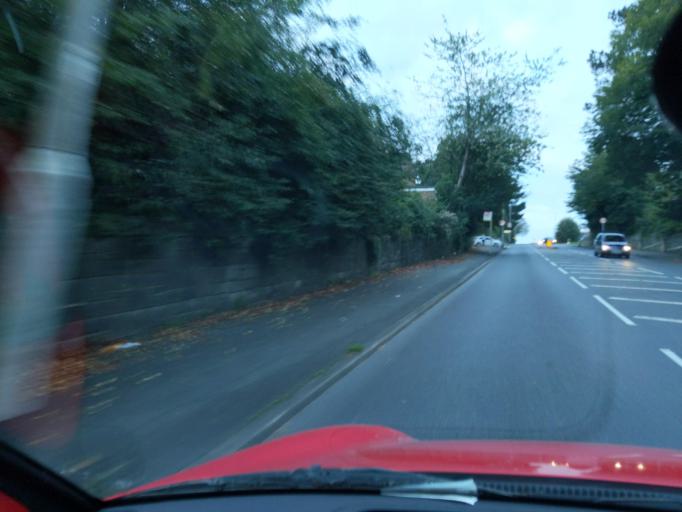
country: GB
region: England
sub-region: Cornwall
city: Millbrook
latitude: 50.3970
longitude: -4.1689
